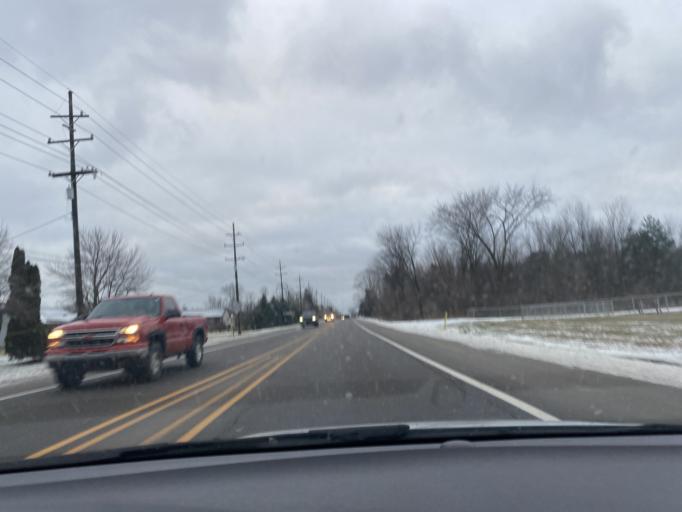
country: US
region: Michigan
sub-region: Lapeer County
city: Imlay City
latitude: 42.9756
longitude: -83.0578
